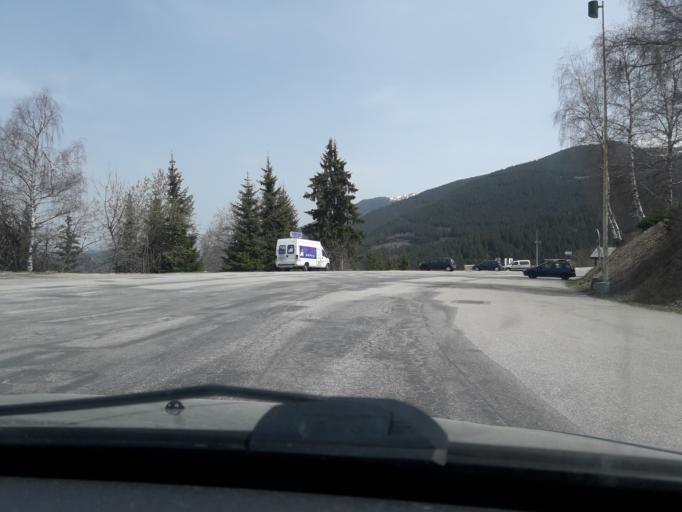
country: FR
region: Rhone-Alpes
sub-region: Departement de l'Isere
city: Theys
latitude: 45.2564
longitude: 5.9924
